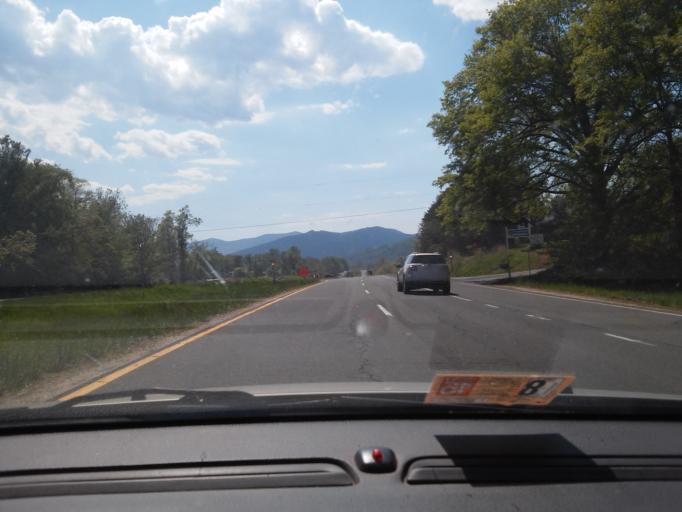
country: US
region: Virginia
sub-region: Rappahannock County
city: Washington
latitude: 38.6881
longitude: -78.1845
